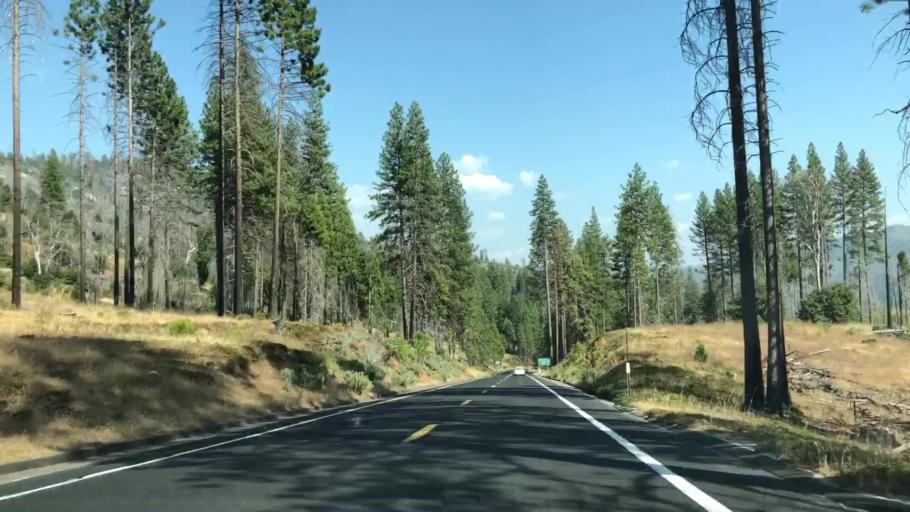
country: US
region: California
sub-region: Mariposa County
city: Midpines
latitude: 37.8222
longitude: -119.9635
